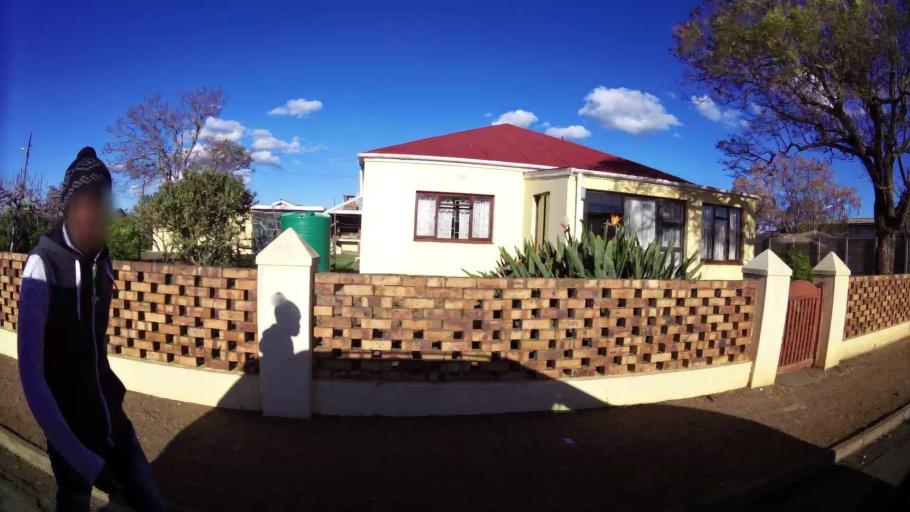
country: ZA
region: Western Cape
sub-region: Eden District Municipality
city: Riversdale
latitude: -34.0995
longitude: 20.9621
